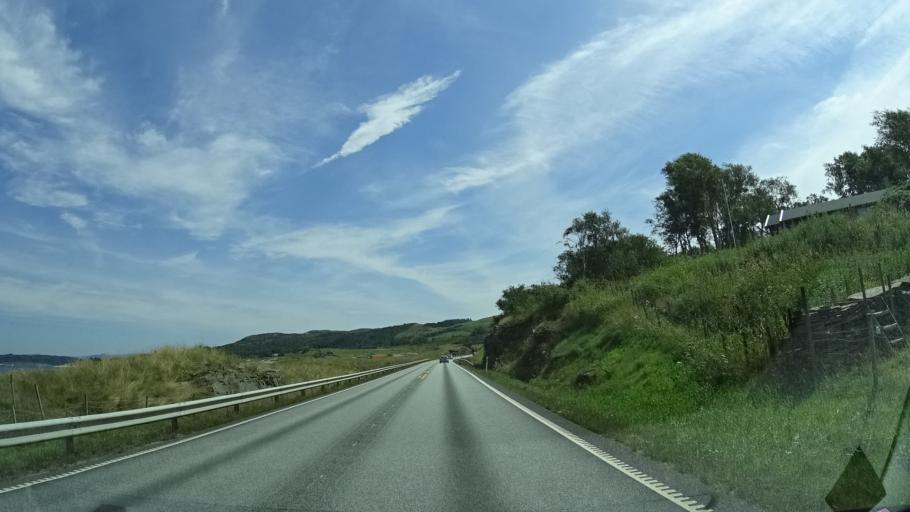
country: NO
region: Rogaland
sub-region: Rennesoy
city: Vikevag
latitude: 59.1205
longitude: 5.6883
